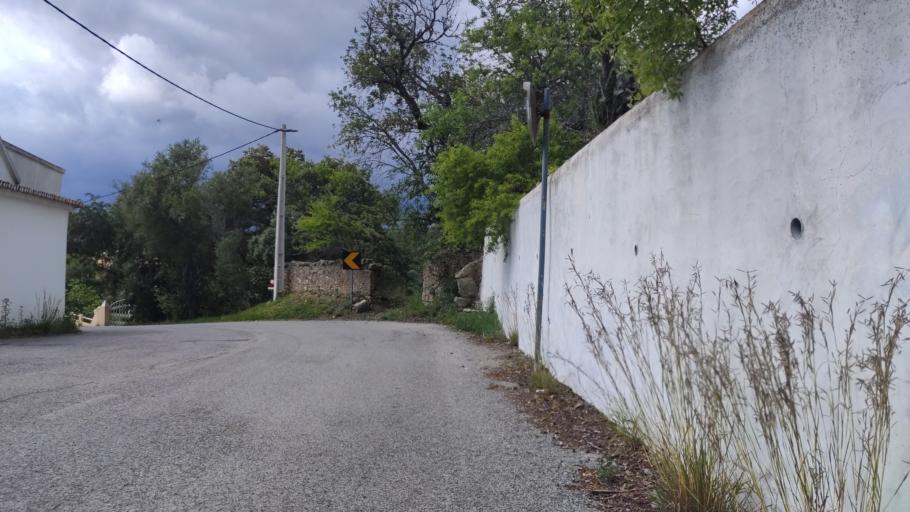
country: PT
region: Faro
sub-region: Sao Bras de Alportel
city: Sao Bras de Alportel
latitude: 37.1593
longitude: -7.9409
